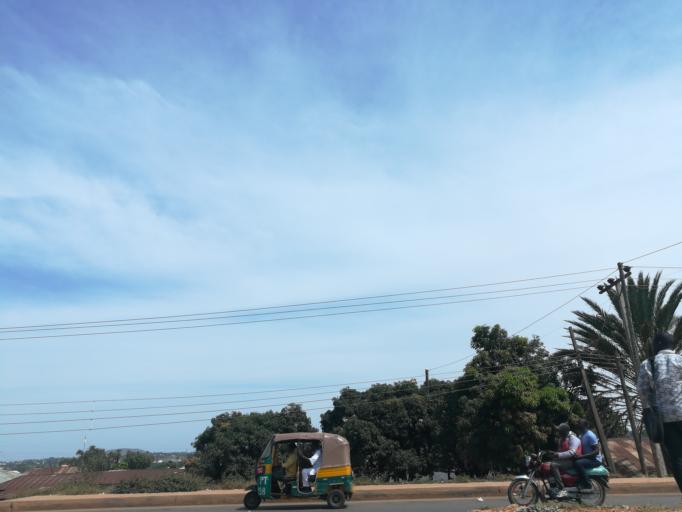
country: NG
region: Plateau
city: Bukuru
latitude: 9.7681
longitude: 8.8601
